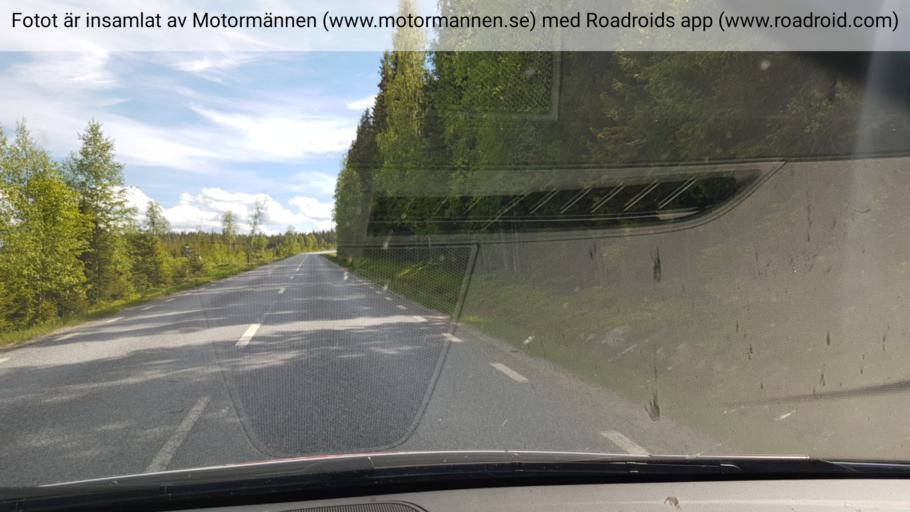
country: SE
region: Vaesterbotten
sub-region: Skelleftea Kommun
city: Burtraesk
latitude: 64.4160
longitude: 20.3953
